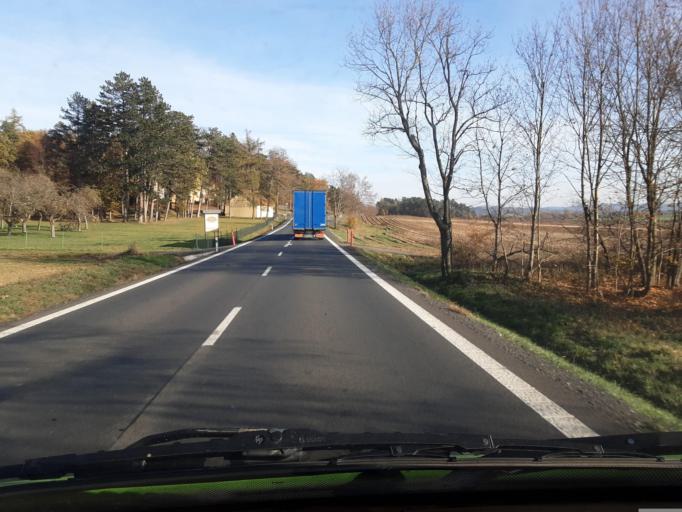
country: CZ
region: Plzensky
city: Hradek
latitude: 49.3297
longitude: 13.5740
